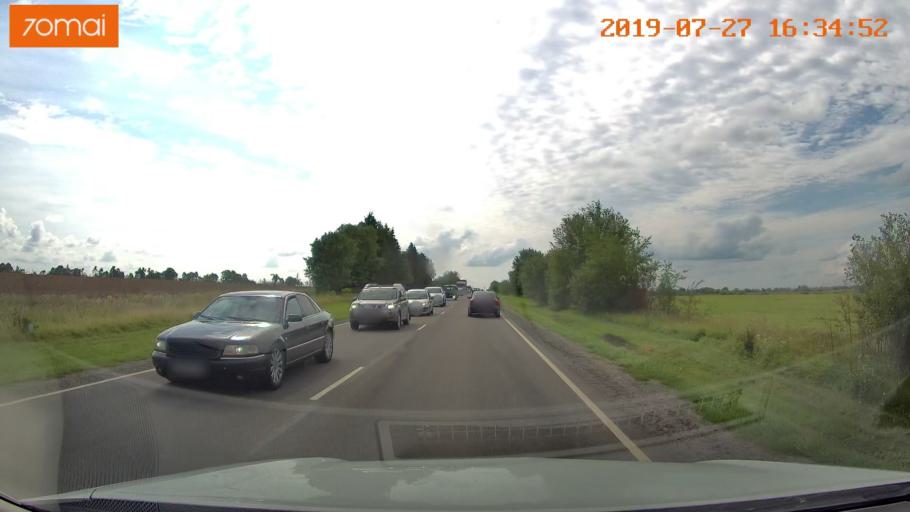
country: RU
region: Kaliningrad
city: Gvardeysk
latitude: 54.6498
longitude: 21.3192
